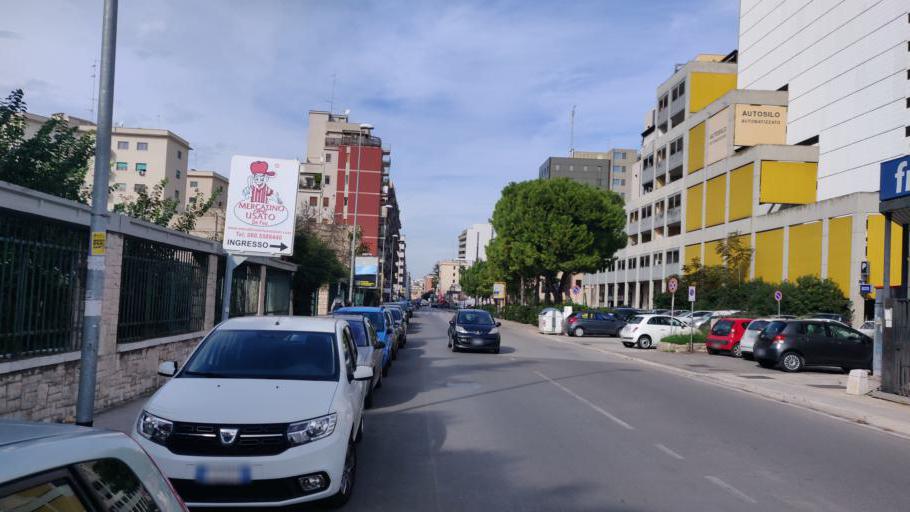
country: IT
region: Apulia
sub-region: Provincia di Bari
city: Bari
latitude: 41.1119
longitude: 16.8824
